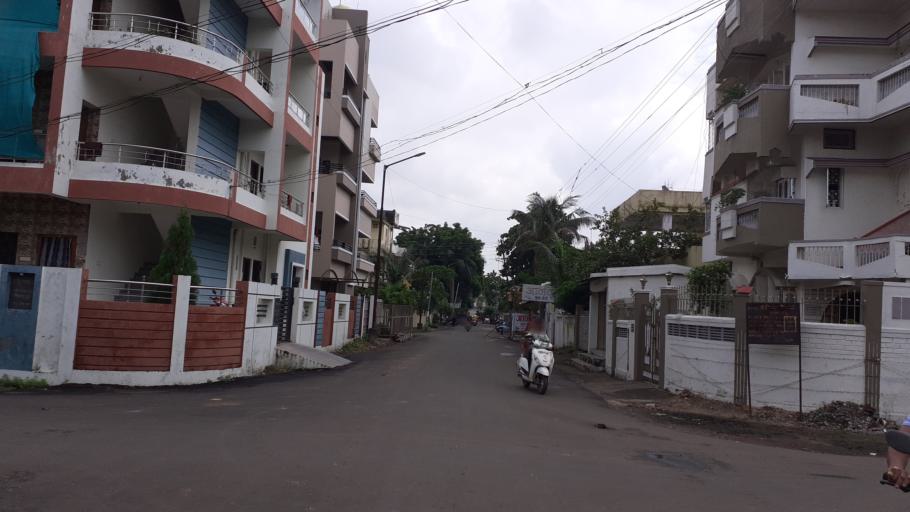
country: IN
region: Maharashtra
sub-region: Nagpur Division
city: Nagpur
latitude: 21.1305
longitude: 79.1136
